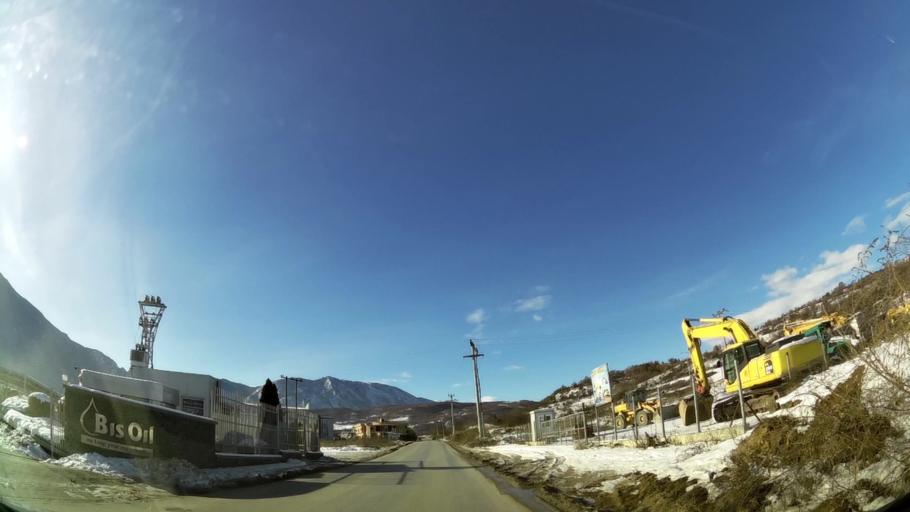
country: MK
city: Ljubin
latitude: 41.9893
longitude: 21.3113
